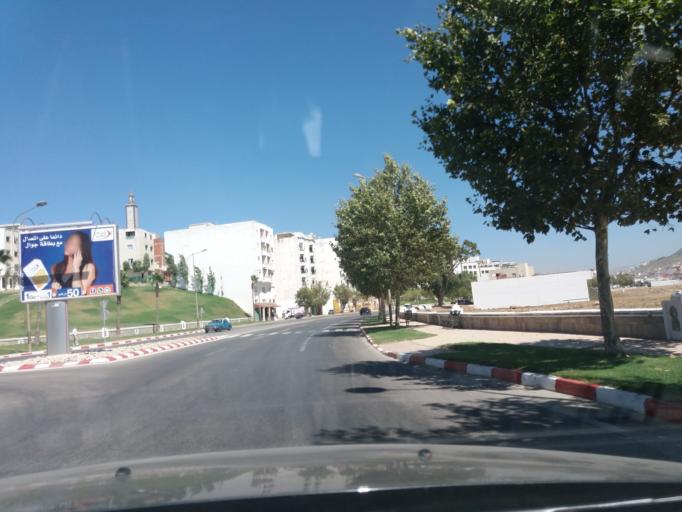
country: MA
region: Tanger-Tetouan
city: Tetouan
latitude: 35.5673
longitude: -5.4058
